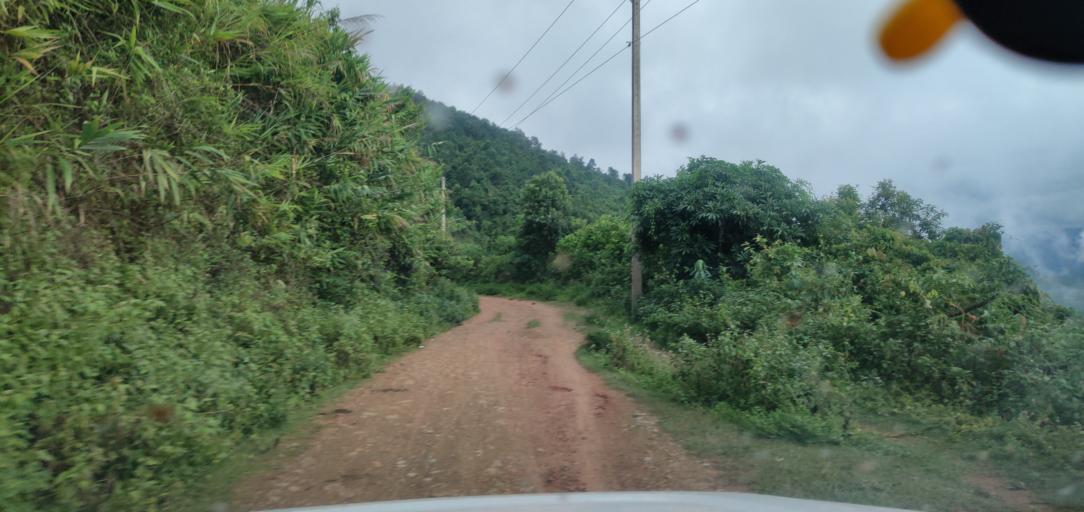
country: LA
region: Phongsali
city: Phongsali
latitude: 21.4472
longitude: 102.2905
